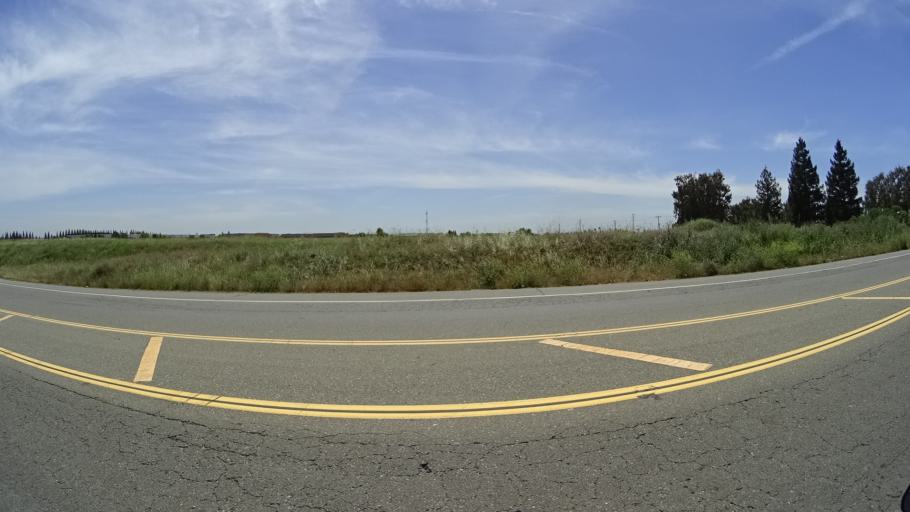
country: US
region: California
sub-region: Placer County
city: Roseville
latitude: 38.8173
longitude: -121.3057
